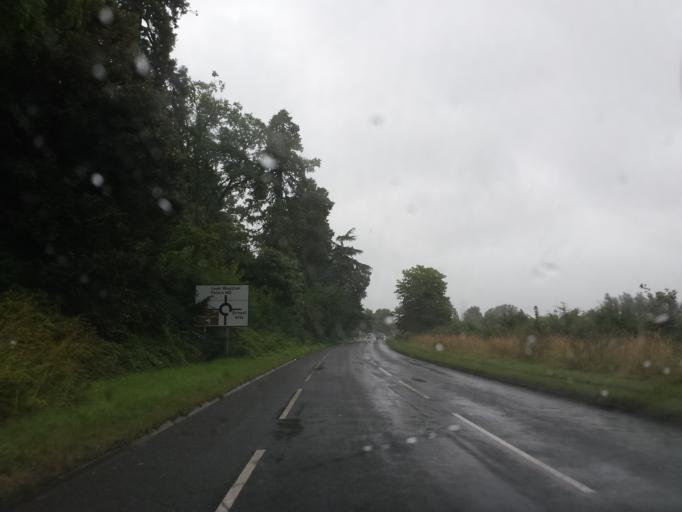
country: GB
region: England
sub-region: Warwickshire
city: Warwick
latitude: 52.3108
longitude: -1.5758
